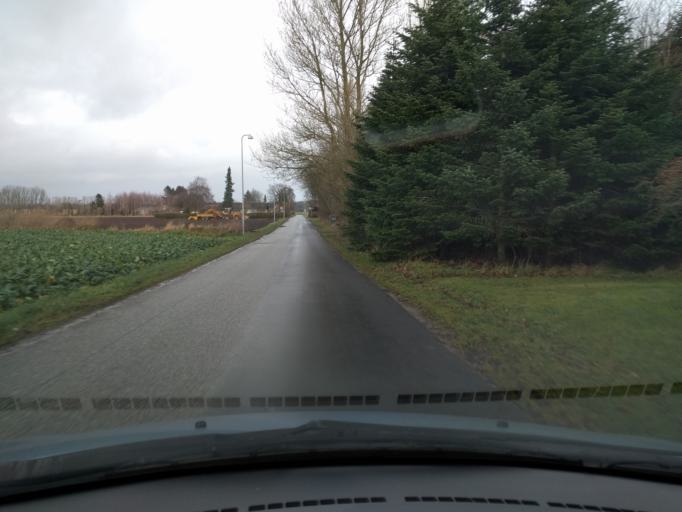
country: DK
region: South Denmark
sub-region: Kerteminde Kommune
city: Langeskov
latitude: 55.3410
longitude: 10.5432
